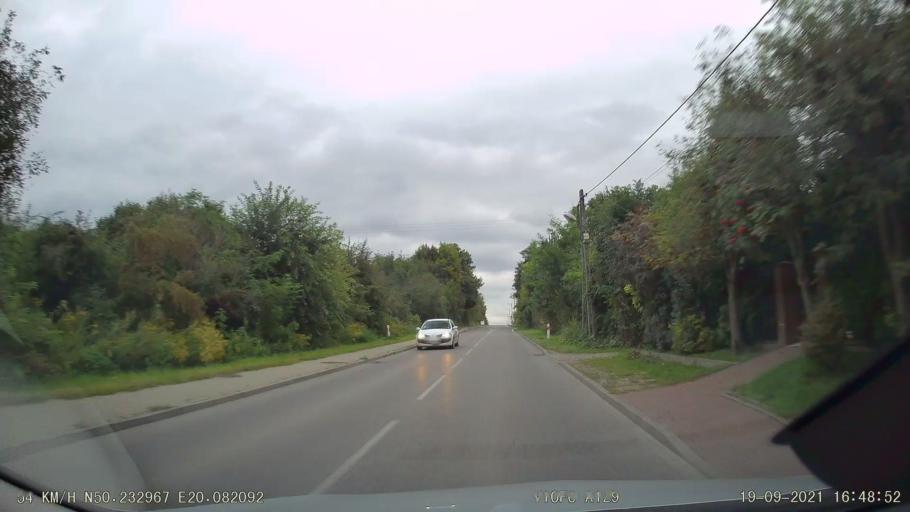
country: PL
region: Lesser Poland Voivodeship
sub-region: Powiat krakowski
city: Slomniki
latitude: 50.2328
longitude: 20.0821
